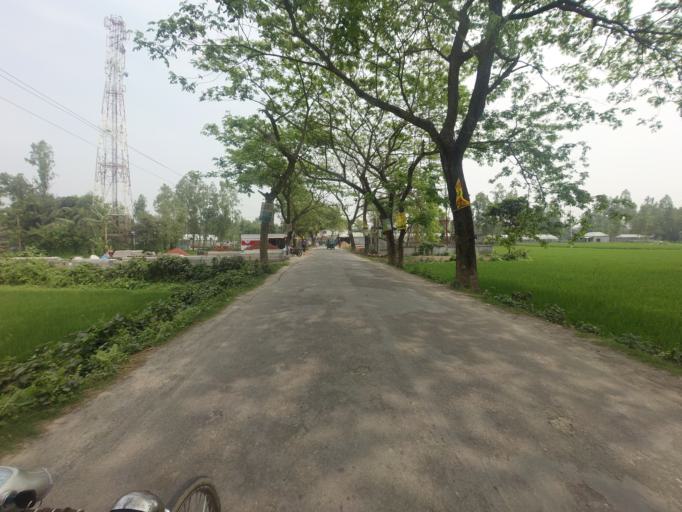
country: BD
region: Rajshahi
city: Sirajganj
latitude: 24.3925
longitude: 89.6890
